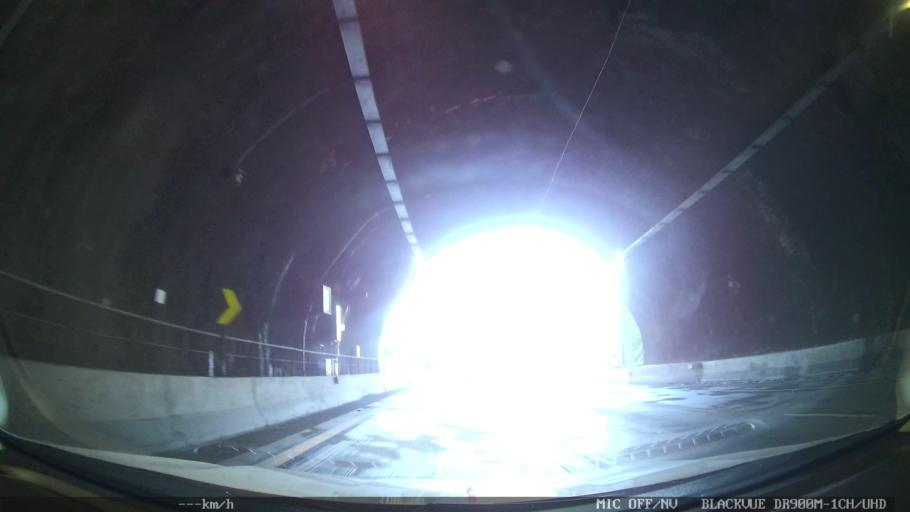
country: BR
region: Sao Paulo
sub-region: Juquitiba
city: Juquitiba
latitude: -24.1020
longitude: -47.2589
